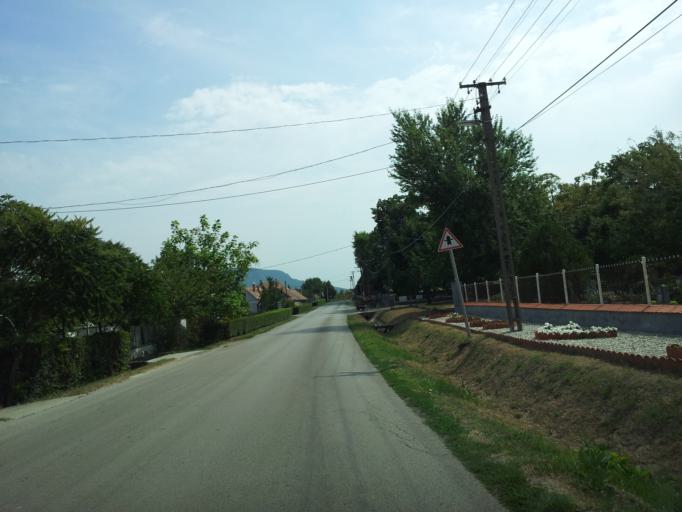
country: HU
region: Veszprem
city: Tapolca
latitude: 46.8446
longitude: 17.4664
